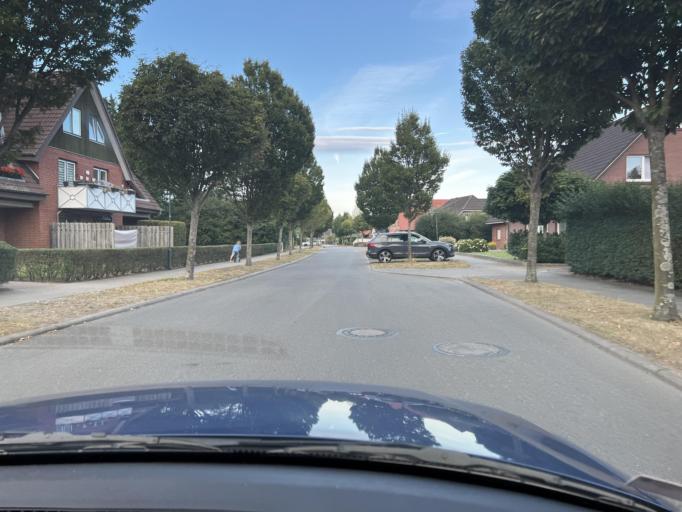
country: DE
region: Schleswig-Holstein
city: Wesseln
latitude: 54.2027
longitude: 9.0800
